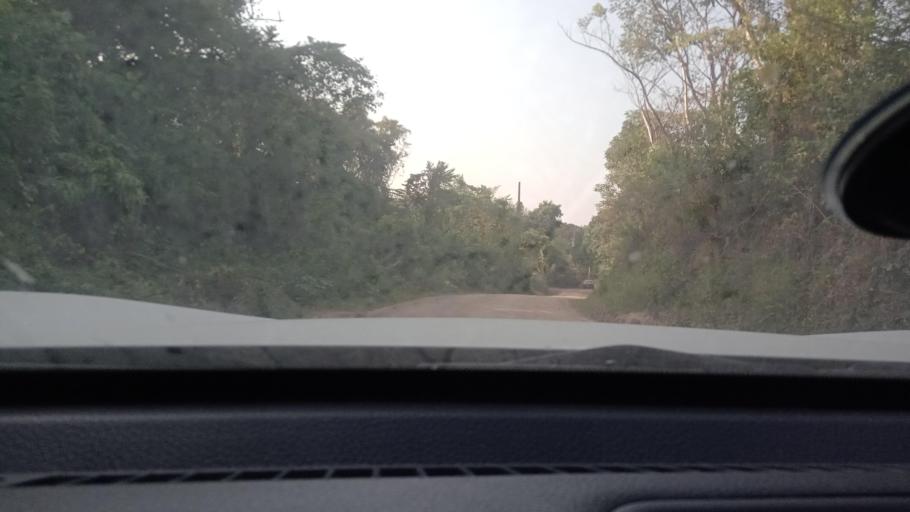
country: MX
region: Tabasco
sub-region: Huimanguillo
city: Francisco Rueda
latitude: 17.6738
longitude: -93.8679
